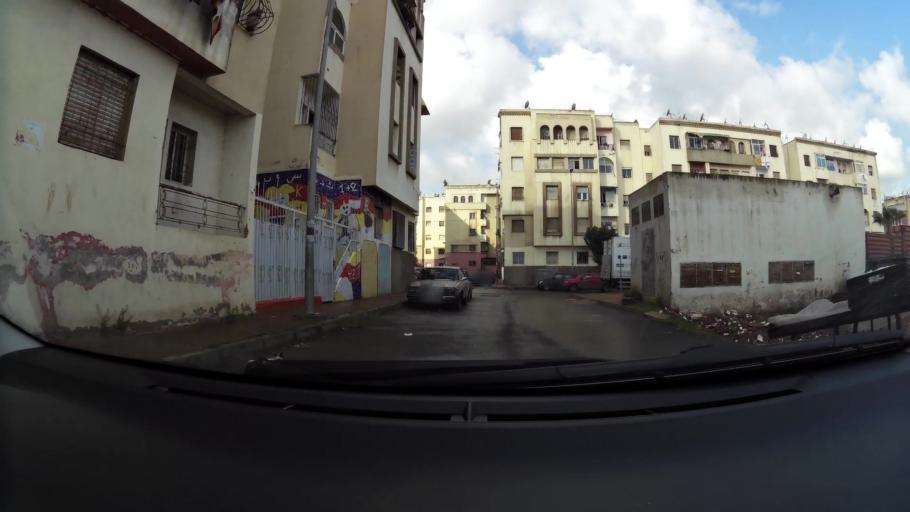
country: MA
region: Grand Casablanca
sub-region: Mediouna
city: Tit Mellil
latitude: 33.5986
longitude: -7.5328
